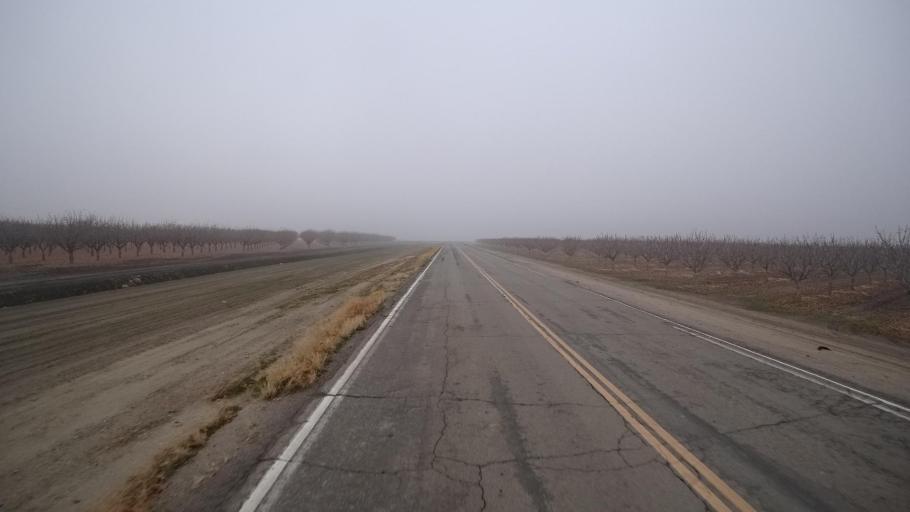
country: US
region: California
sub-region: Kern County
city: Buttonwillow
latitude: 35.4276
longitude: -119.5387
